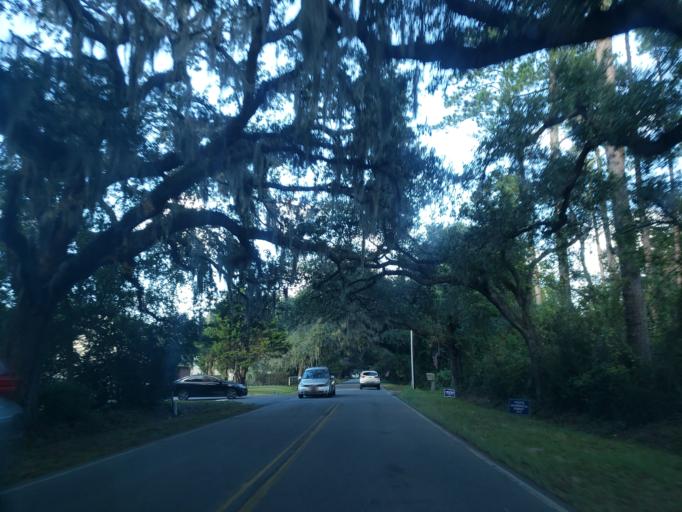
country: US
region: Georgia
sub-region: Chatham County
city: Isle of Hope
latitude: 31.9806
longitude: -81.0785
